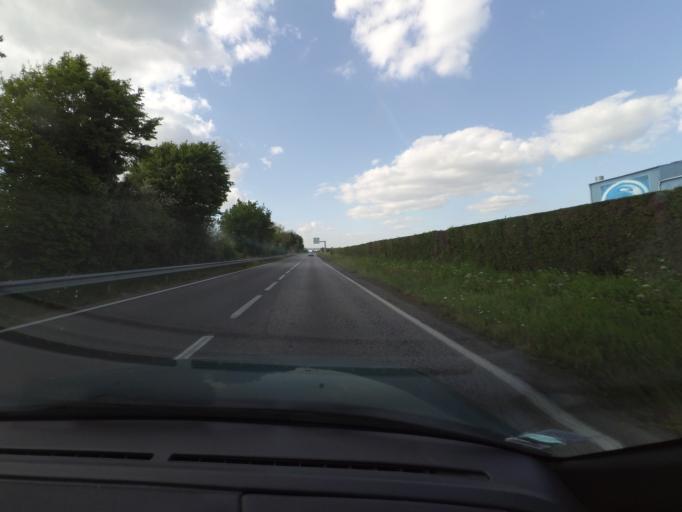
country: FR
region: Pays de la Loire
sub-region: Departement de la Vendee
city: Mouilleron-le-Captif
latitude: 46.7412
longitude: -1.4302
